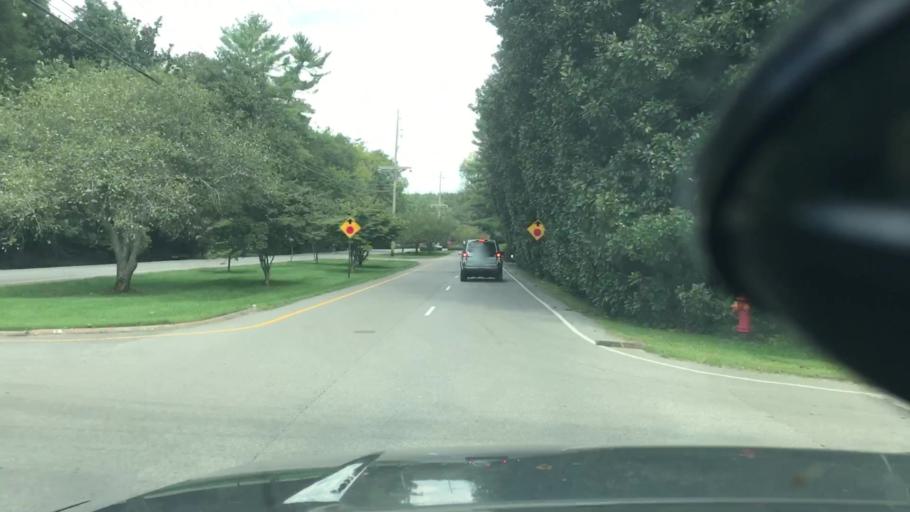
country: US
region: Tennessee
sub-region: Davidson County
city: Belle Meade
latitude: 36.1081
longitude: -86.8569
